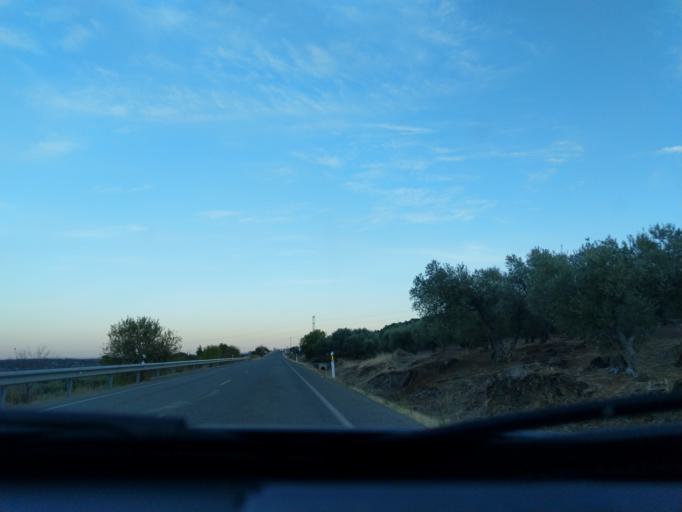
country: ES
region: Extremadura
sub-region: Provincia de Badajoz
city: Reina
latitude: 38.1864
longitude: -5.9381
